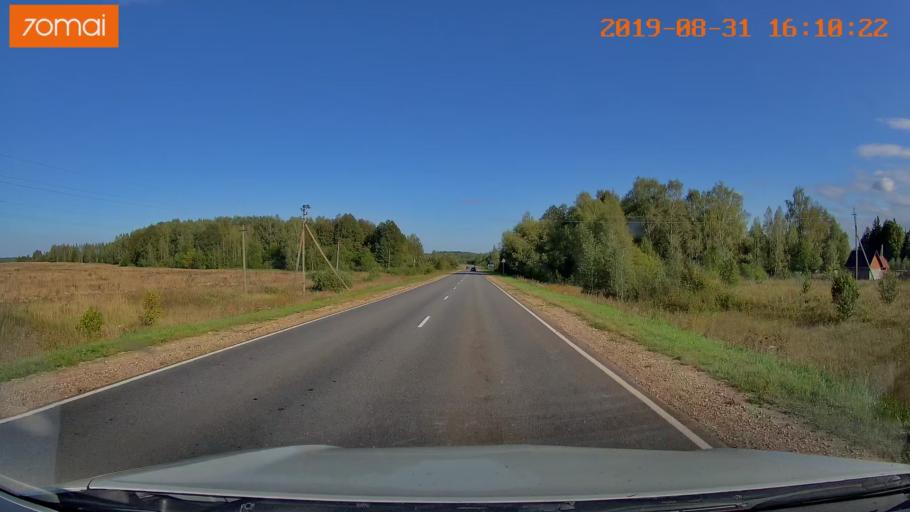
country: RU
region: Kaluga
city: Nikola-Lenivets
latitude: 54.5840
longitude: 35.4238
